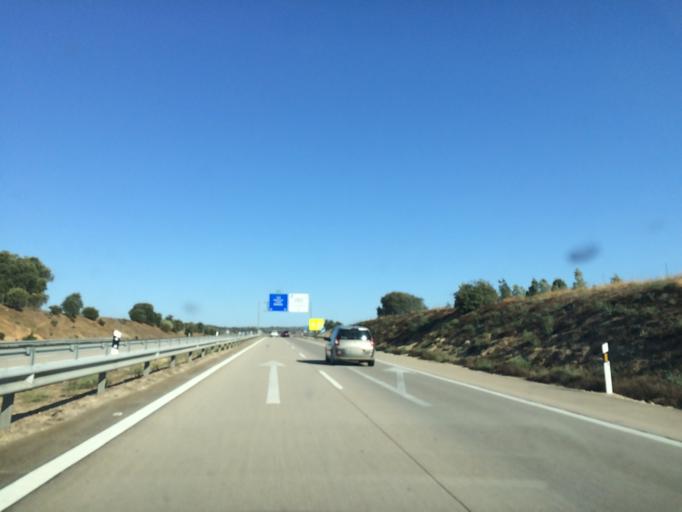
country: ES
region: Castille-La Mancha
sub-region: Province of Toledo
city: Cervera de los Montes
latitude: 40.0097
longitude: -4.7755
